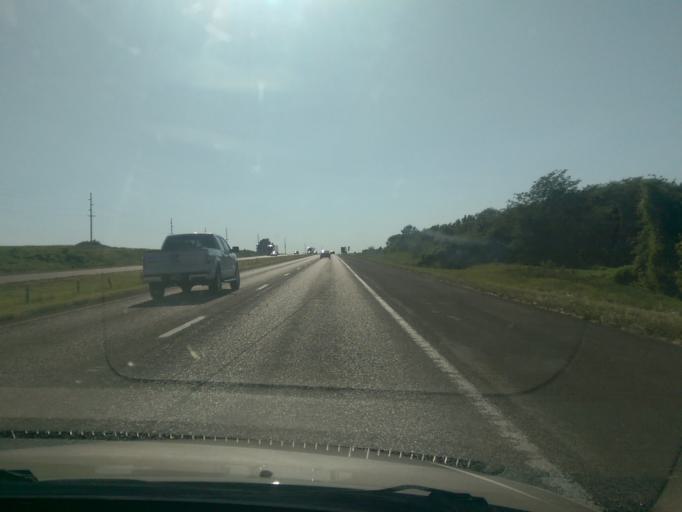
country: US
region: Missouri
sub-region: Lafayette County
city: Higginsville
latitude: 38.9929
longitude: -93.7025
